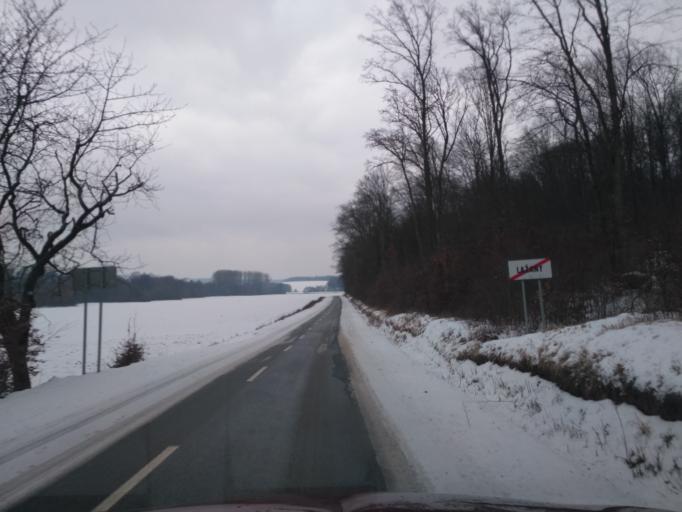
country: SK
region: Presovsky
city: Sabinov
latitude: 49.0405
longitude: 21.0990
